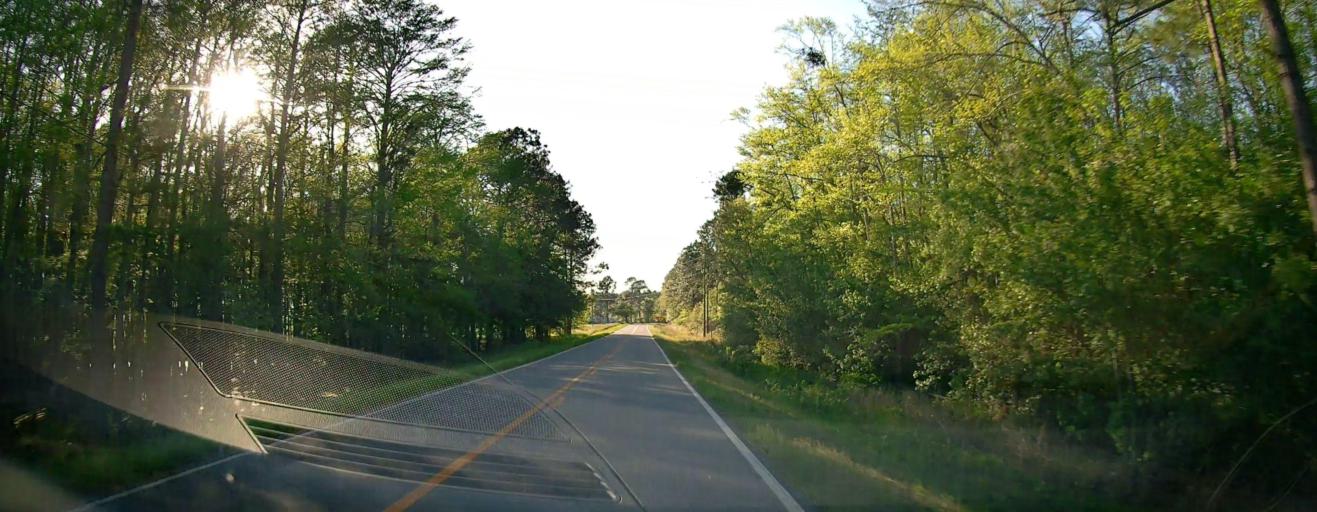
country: US
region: Georgia
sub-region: Ben Hill County
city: Fitzgerald
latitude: 31.6854
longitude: -83.2095
